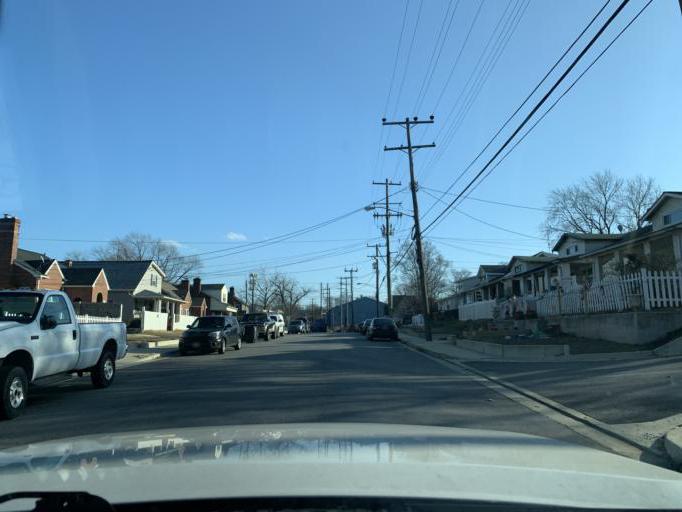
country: US
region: Maryland
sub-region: Prince George's County
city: Fairmount Heights
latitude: 38.9135
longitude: -76.9323
